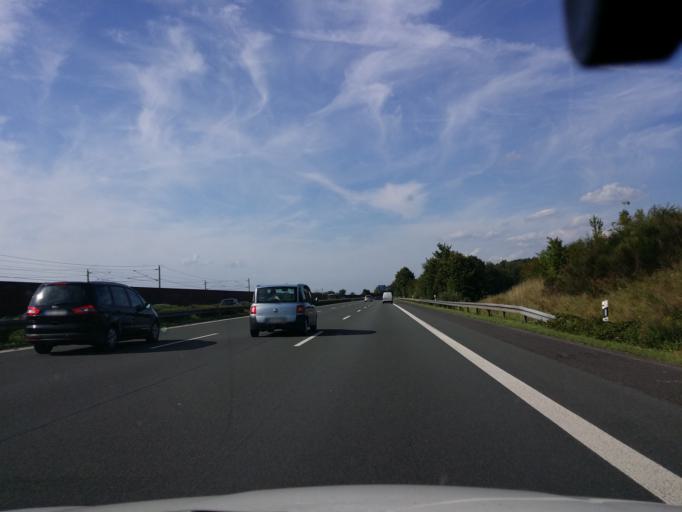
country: DE
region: North Rhine-Westphalia
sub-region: Regierungsbezirk Koln
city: Stossdorf
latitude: 50.7522
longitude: 7.2328
